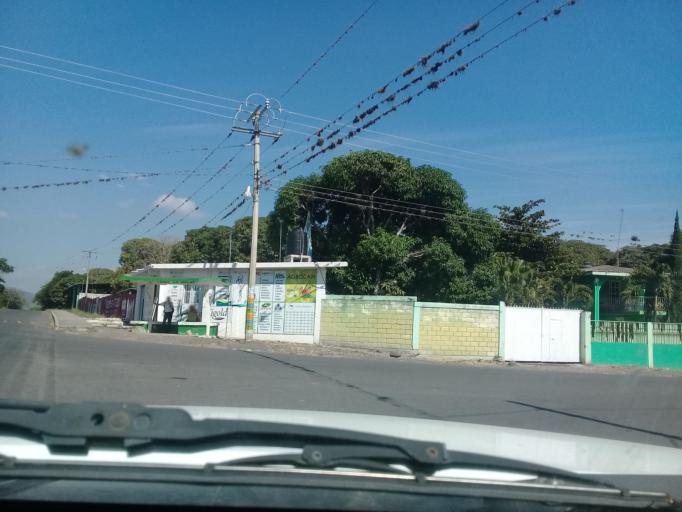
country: MX
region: Veracruz
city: Actopan
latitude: 19.4747
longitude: -96.5785
